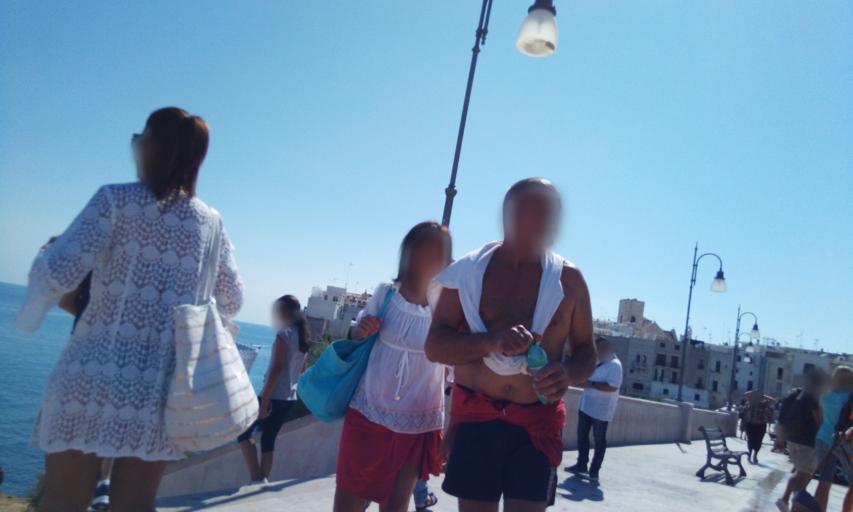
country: IT
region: Apulia
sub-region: Provincia di Bari
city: Polignano a Mare
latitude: 40.9974
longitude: 17.2171
